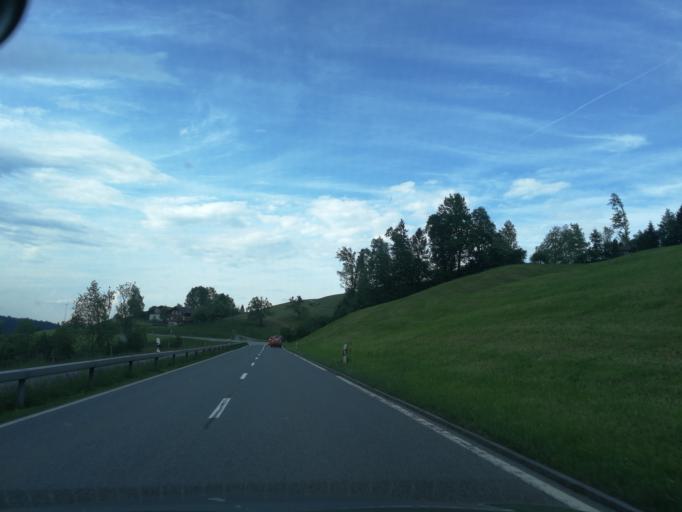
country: CH
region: Lucerne
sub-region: Entlebuch District
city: Entlebuch
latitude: 47.0170
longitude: 8.0762
